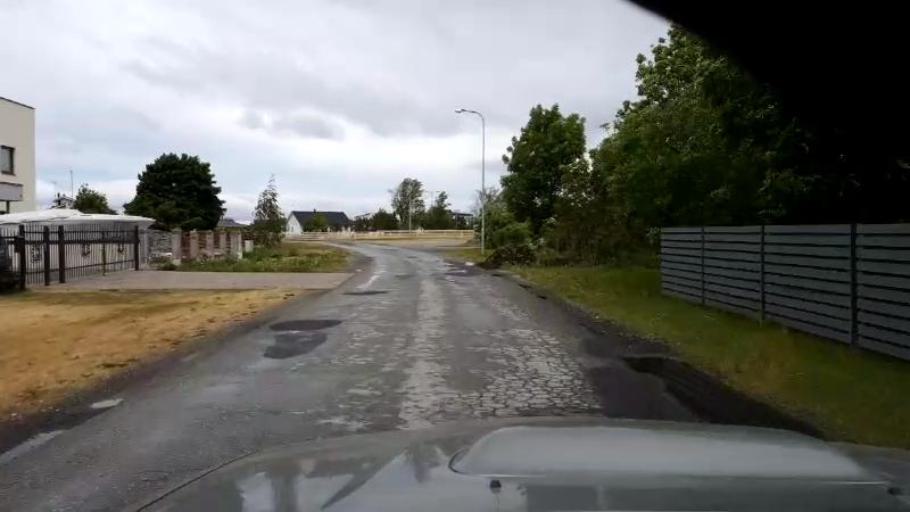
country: EE
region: Harju
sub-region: Harku vald
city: Tabasalu
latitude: 59.4581
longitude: 24.4512
